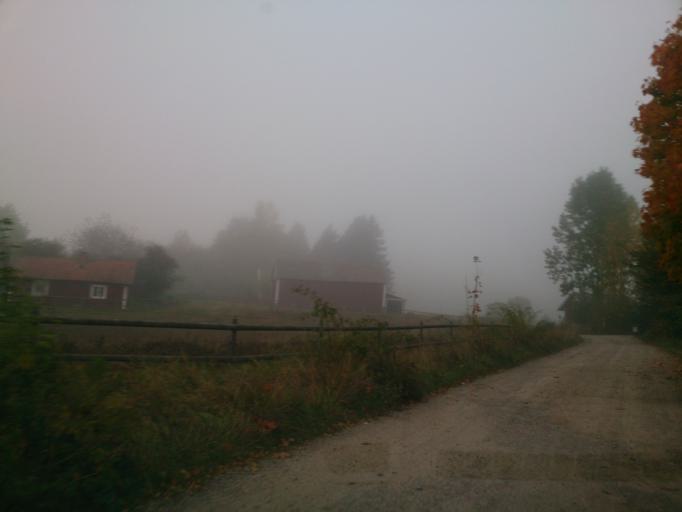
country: SE
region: OEstergoetland
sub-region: Kinda Kommun
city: Rimforsa
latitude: 58.1303
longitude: 15.6757
